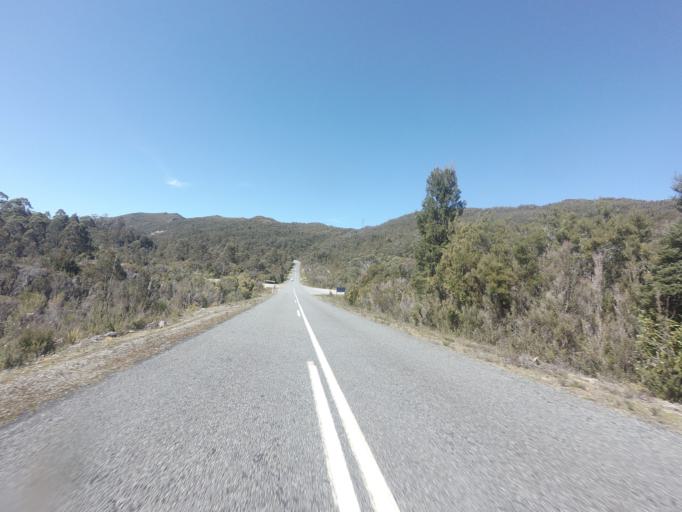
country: AU
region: Tasmania
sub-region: Huon Valley
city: Geeveston
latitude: -42.8143
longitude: 146.3847
